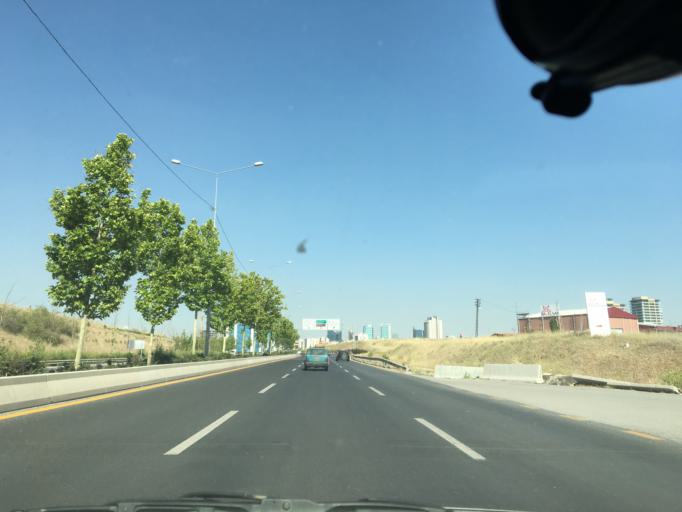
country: TR
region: Ankara
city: Batikent
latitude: 39.9167
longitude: 32.7723
